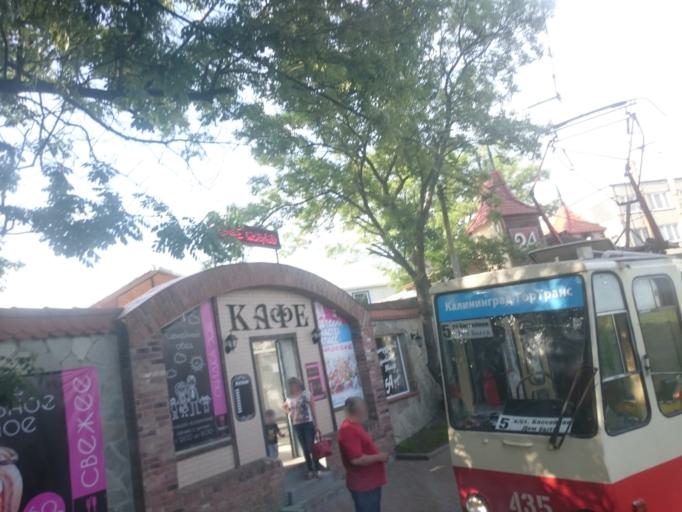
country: RU
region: Kaliningrad
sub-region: Gorod Kaliningrad
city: Kaliningrad
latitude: 54.7211
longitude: 20.4503
